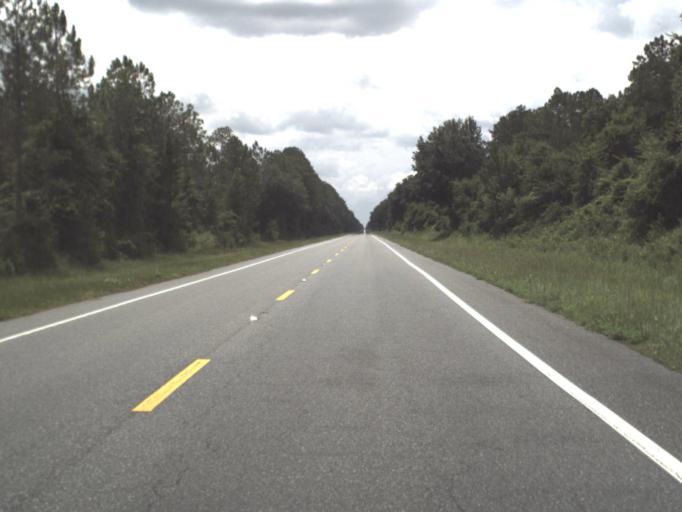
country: US
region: Florida
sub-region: Columbia County
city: Watertown
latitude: 30.1285
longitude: -82.5209
